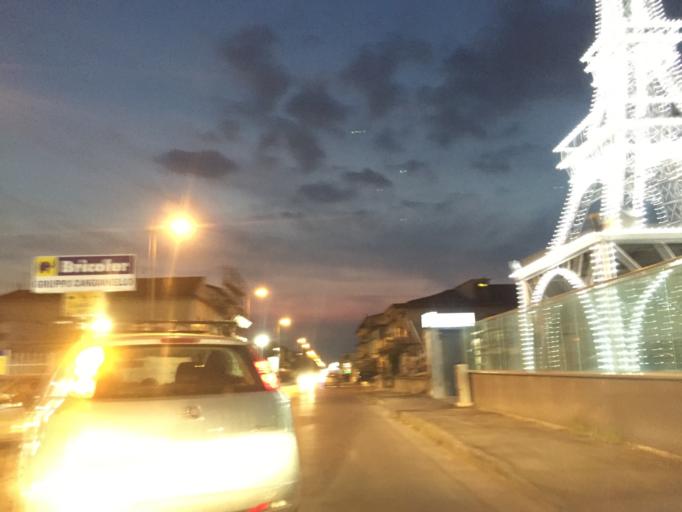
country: IT
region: Campania
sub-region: Provincia di Salerno
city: San Lorenzo
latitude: 40.7479
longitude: 14.5950
